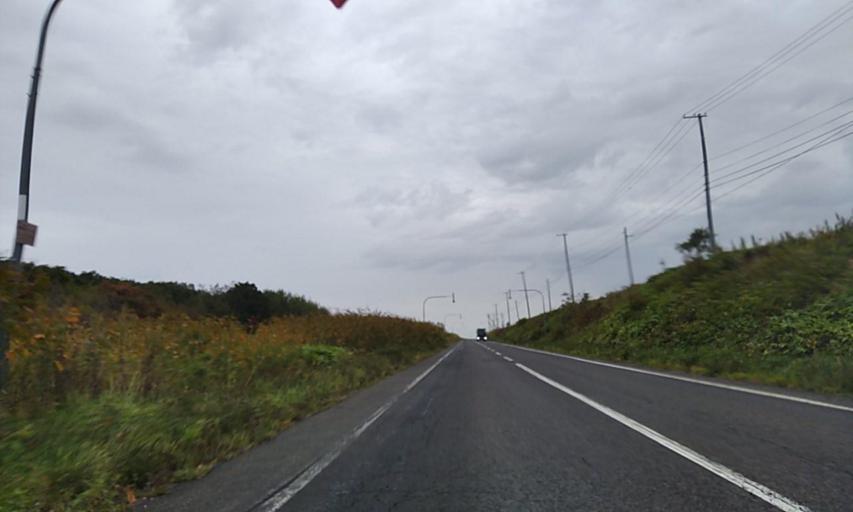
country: JP
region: Hokkaido
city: Mombetsu
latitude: 44.5396
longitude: 143.0230
